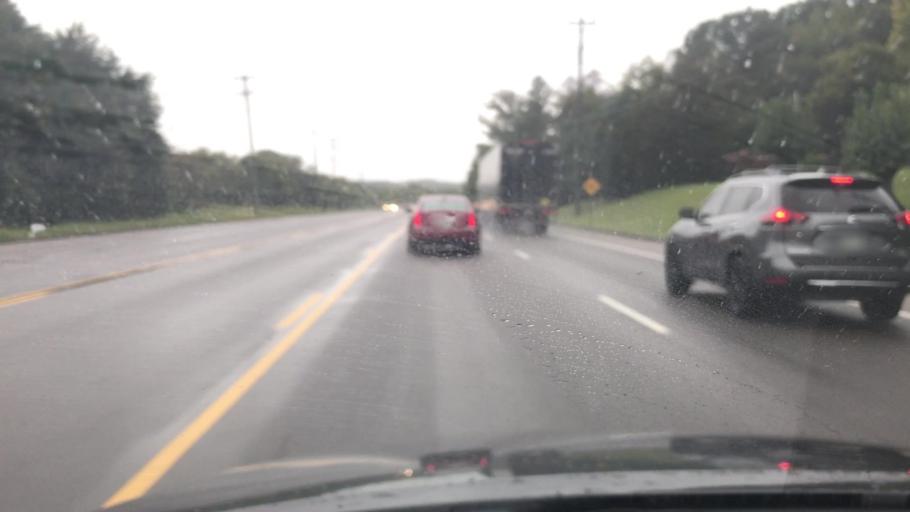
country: US
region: Tennessee
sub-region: Davidson County
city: Belle Meade
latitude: 36.2071
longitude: -86.9372
